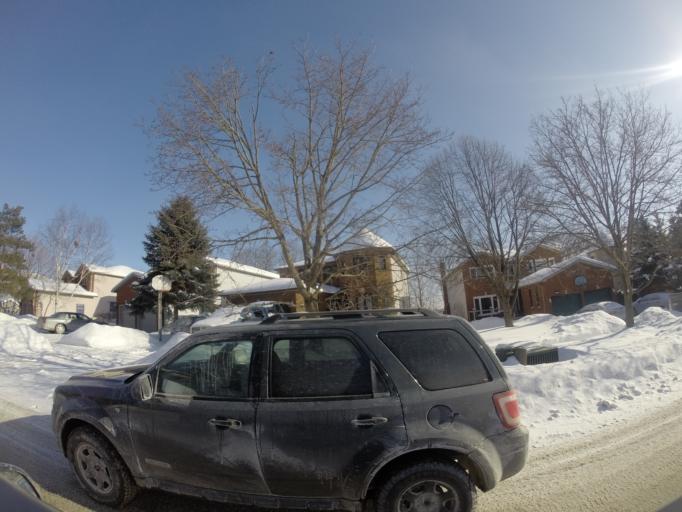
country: CA
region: Ontario
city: Barrie
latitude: 44.3845
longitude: -79.7229
